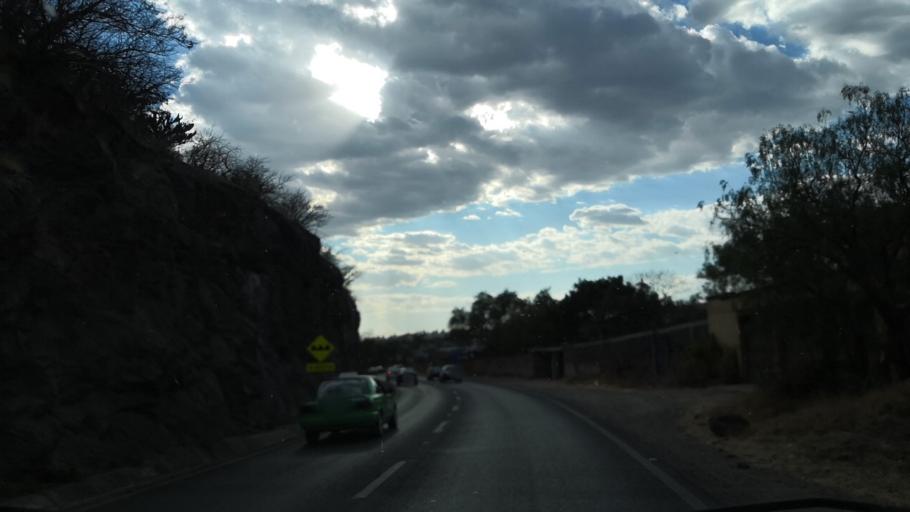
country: MX
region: Guanajuato
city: Marfil
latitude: 21.0009
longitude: -101.2827
